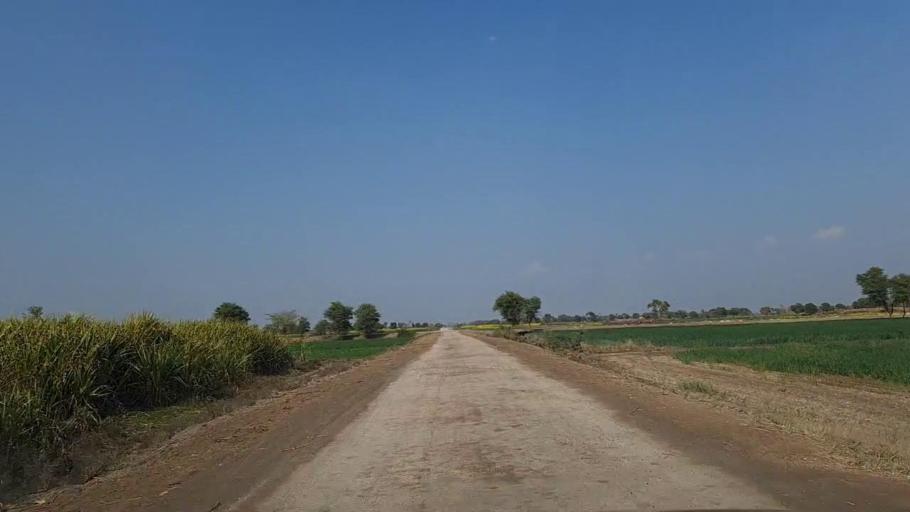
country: PK
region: Sindh
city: Jam Sahib
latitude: 26.2869
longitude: 68.5830
